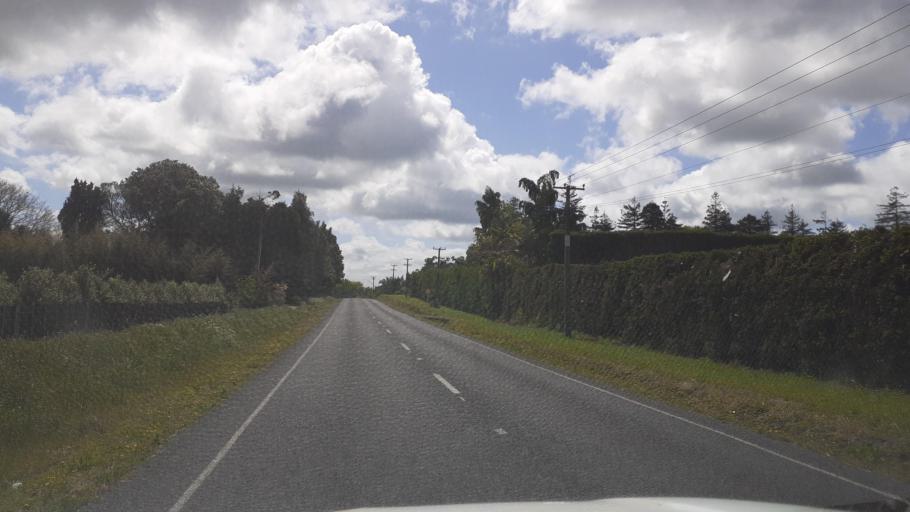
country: NZ
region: Northland
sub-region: Far North District
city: Kerikeri
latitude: -35.2239
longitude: 173.9735
